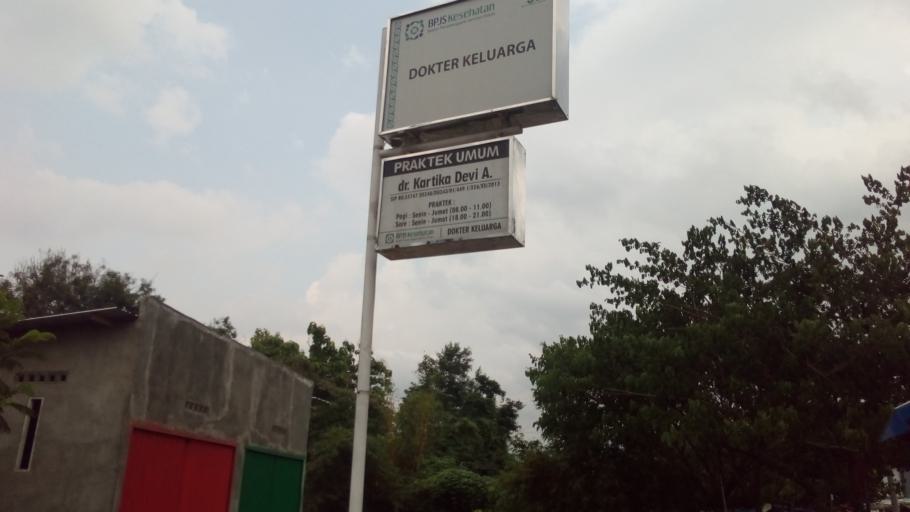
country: ID
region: Central Java
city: Mranggen
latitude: -7.0565
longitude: 110.4714
